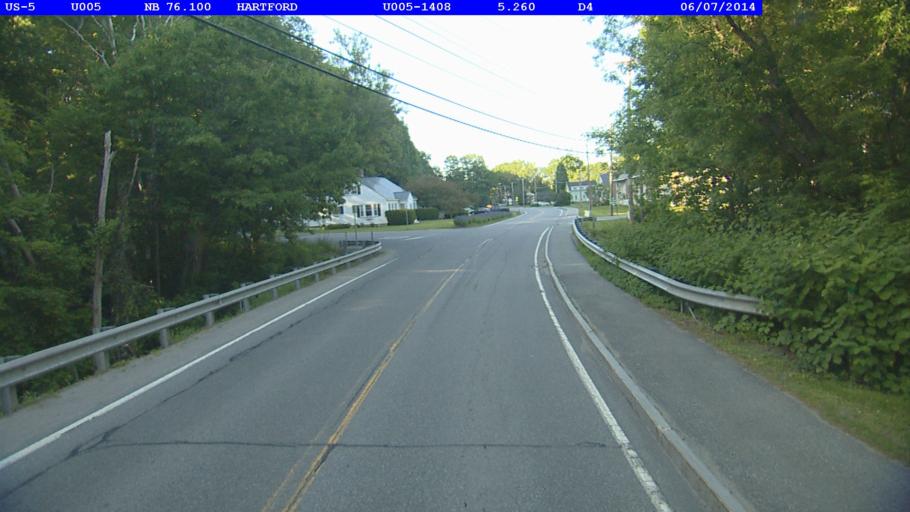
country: US
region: Vermont
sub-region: Windsor County
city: Wilder
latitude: 43.6679
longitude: -72.3117
